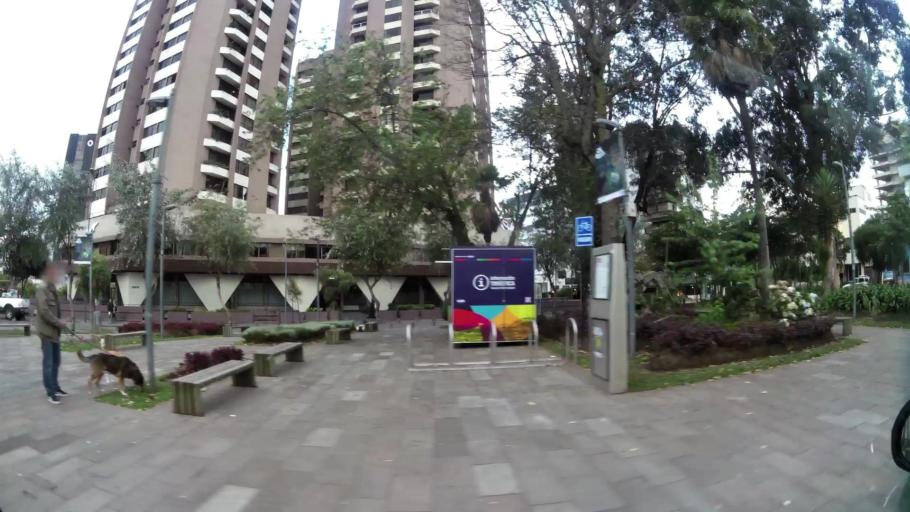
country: EC
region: Pichincha
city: Quito
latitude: -0.2023
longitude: -78.4888
